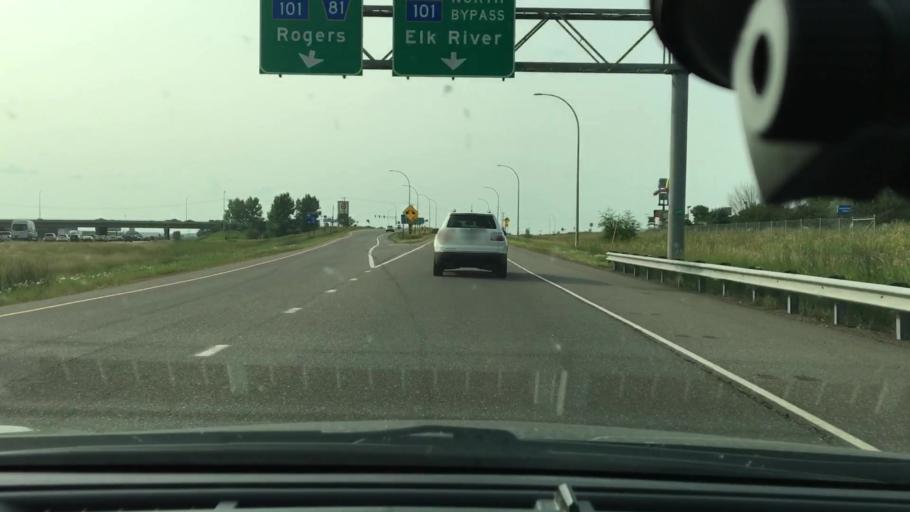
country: US
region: Minnesota
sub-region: Hennepin County
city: Rogers
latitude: 45.1935
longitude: -93.5484
